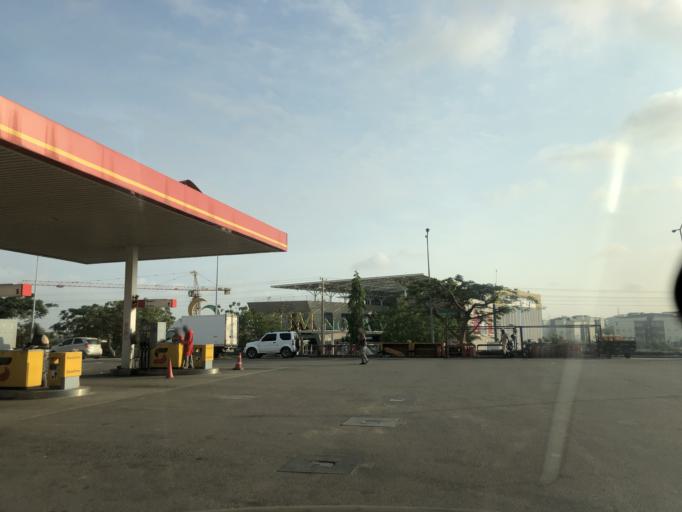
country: AO
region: Luanda
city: Luanda
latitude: -8.8975
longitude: 13.2290
